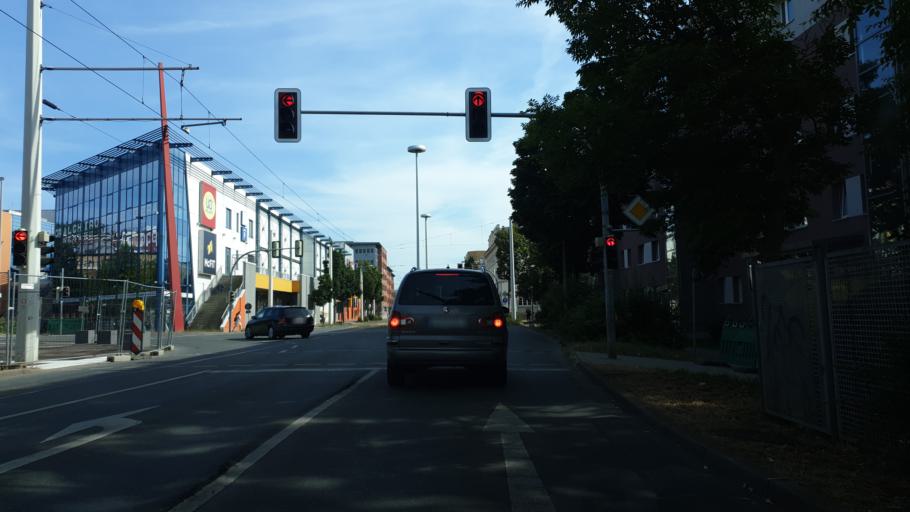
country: DE
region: Thuringia
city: Gera
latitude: 50.8747
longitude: 12.0814
